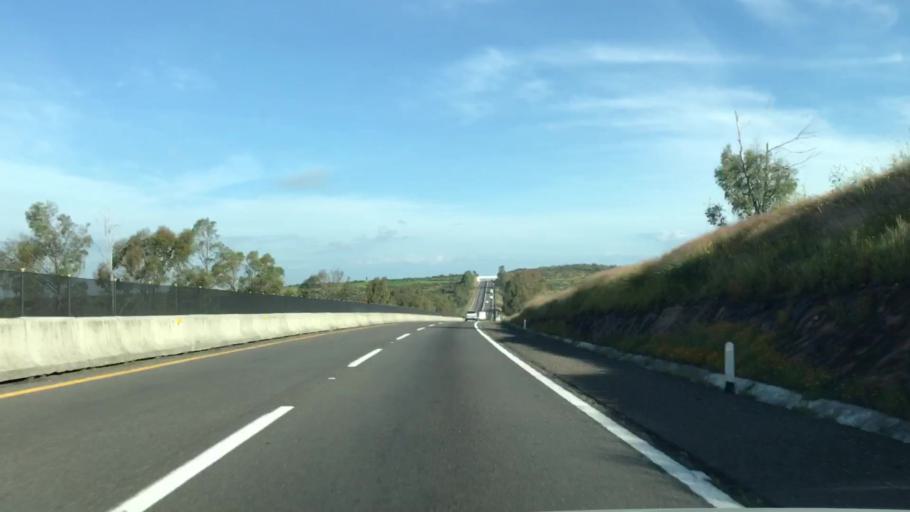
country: MX
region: Jalisco
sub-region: Lagos de Moreno
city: Cristeros [Fraccionamiento]
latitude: 21.3741
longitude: -102.1347
